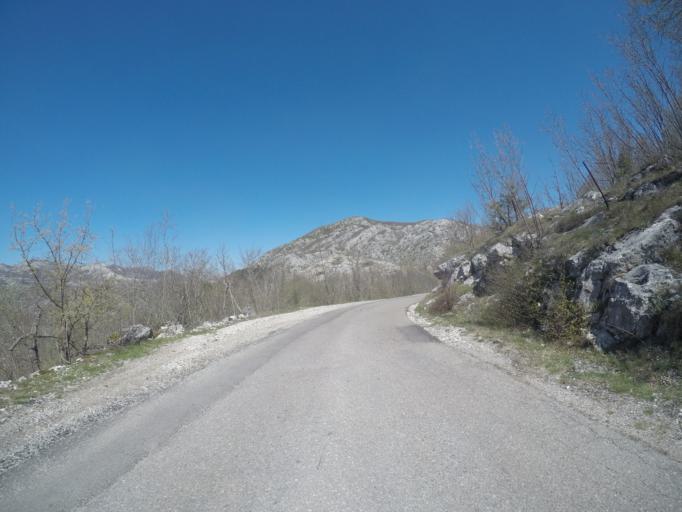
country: ME
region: Cetinje
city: Cetinje
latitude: 42.4556
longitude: 18.8737
